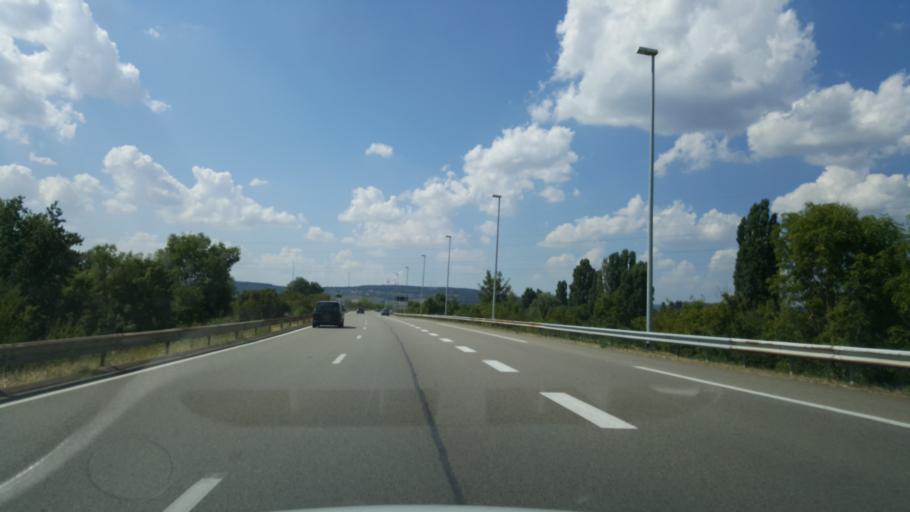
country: FR
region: Bourgogne
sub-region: Departement de la Cote-d'Or
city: Beaune
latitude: 47.0333
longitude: 4.8686
